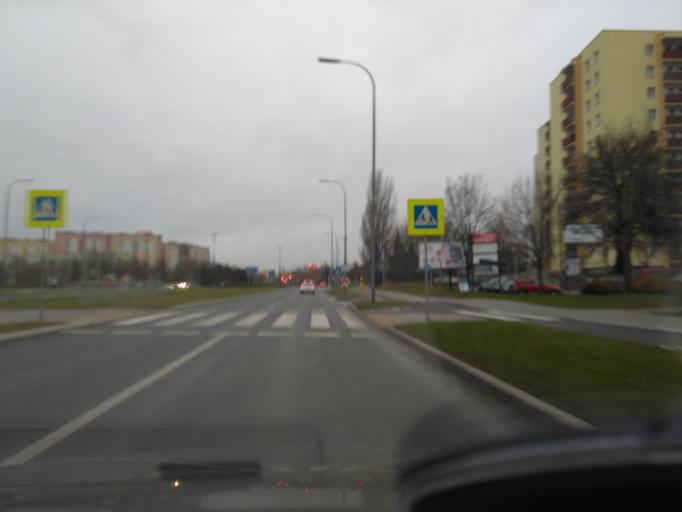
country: PL
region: Lublin Voivodeship
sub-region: Powiat lubelski
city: Lublin
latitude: 51.2606
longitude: 22.5528
